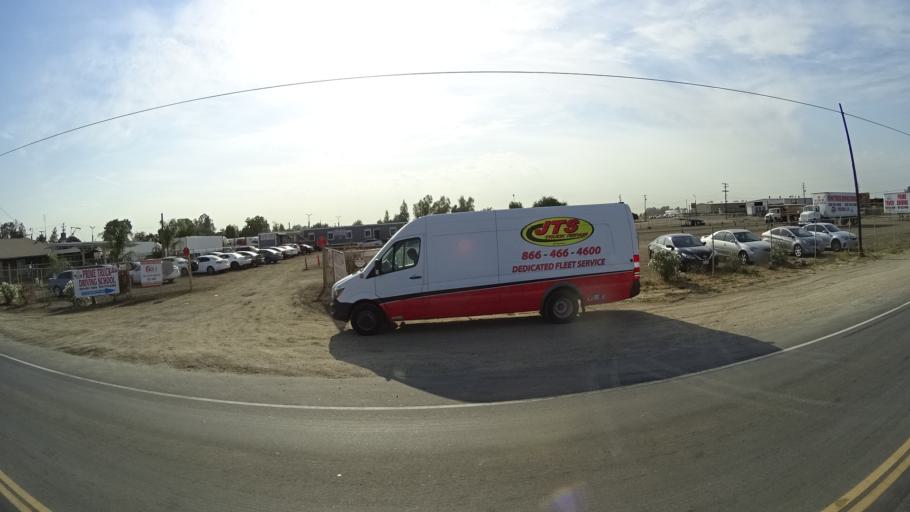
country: US
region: California
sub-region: Fresno County
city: West Park
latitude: 36.7492
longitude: -119.8622
